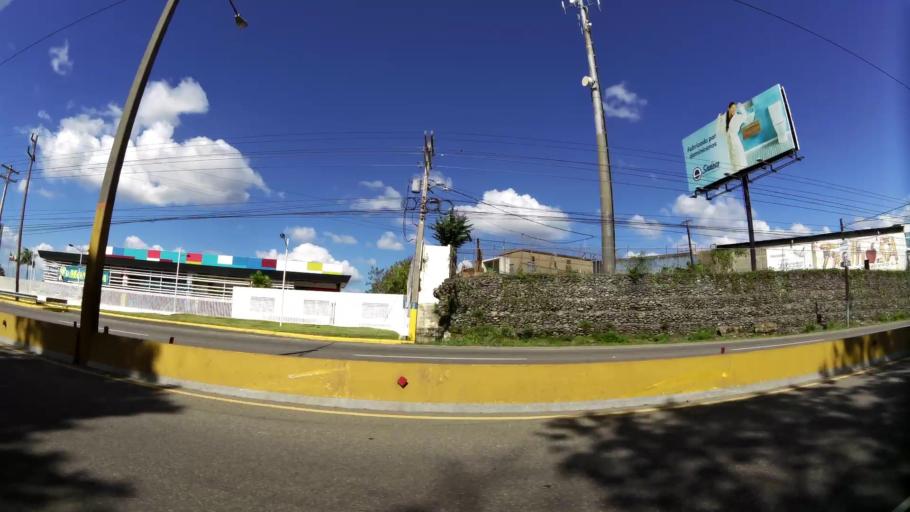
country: DO
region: Santo Domingo
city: Santo Domingo Oeste
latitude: 18.5592
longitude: -70.0590
